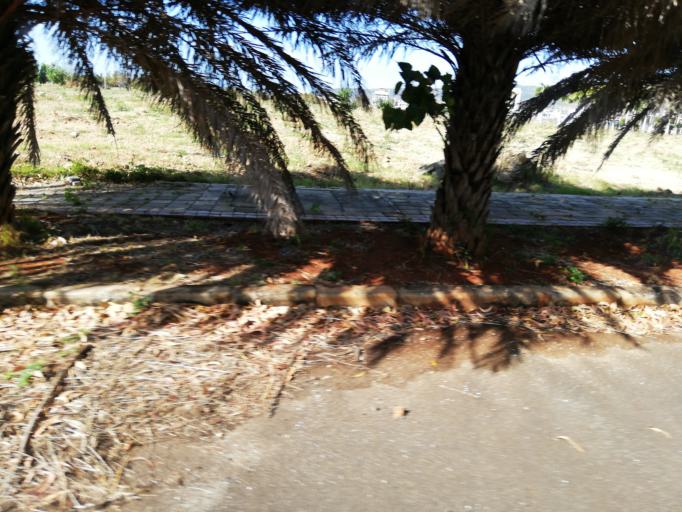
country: MU
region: Port Louis
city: Port Louis
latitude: -20.1591
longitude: 57.4914
